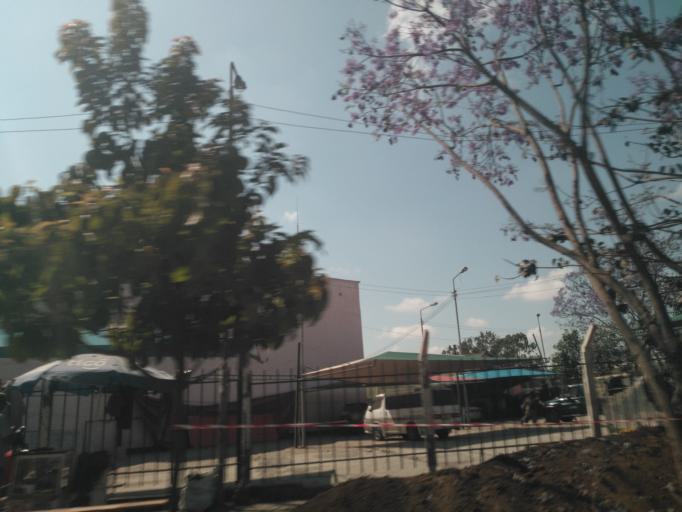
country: TZ
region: Arusha
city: Arusha
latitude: -3.3732
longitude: 36.6927
